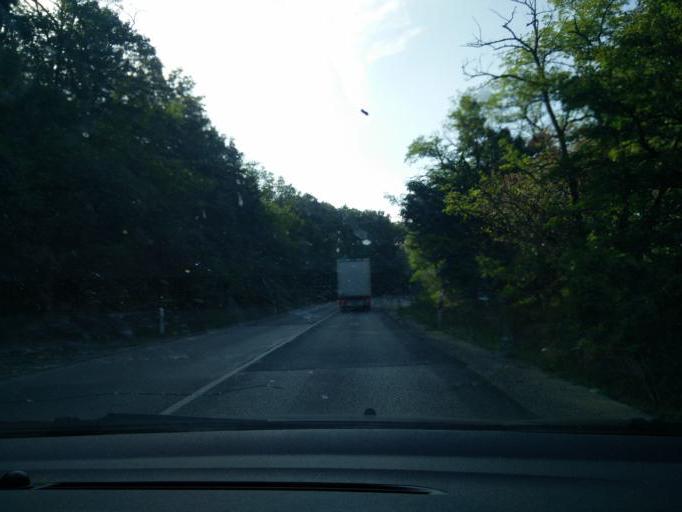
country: HU
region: Pest
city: Pilisszentivan
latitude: 47.6211
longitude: 18.8671
